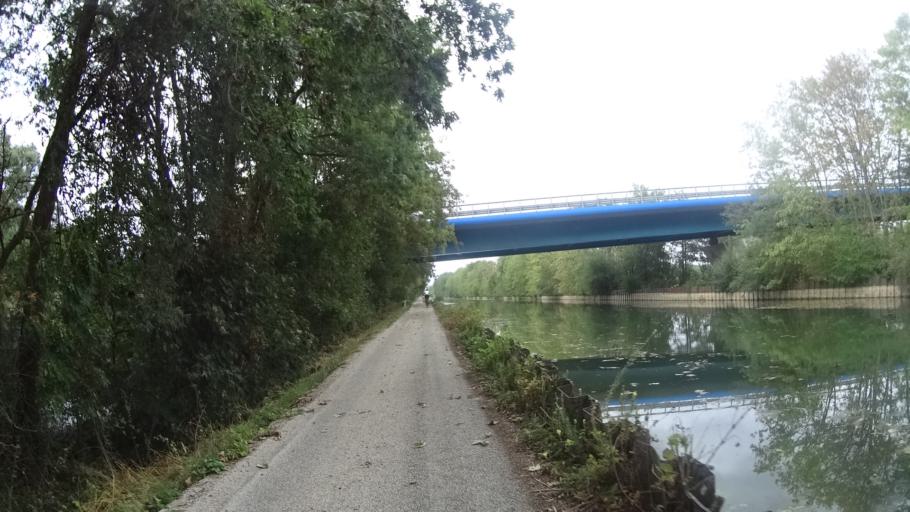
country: FR
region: Picardie
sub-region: Departement de l'Aisne
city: Itancourt
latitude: 49.7537
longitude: 3.3778
